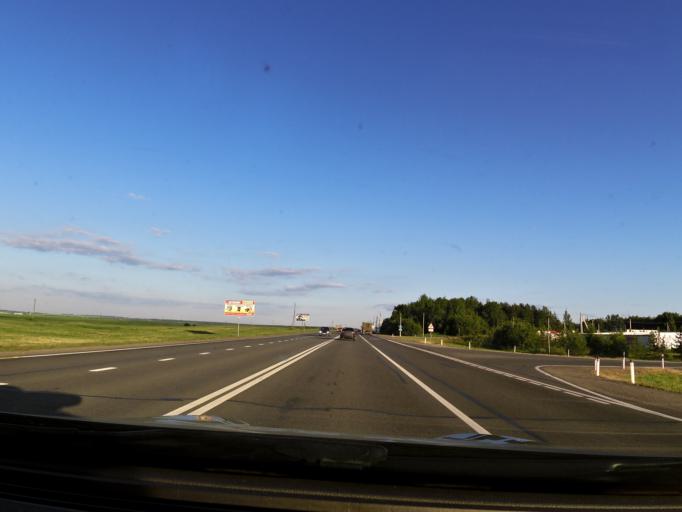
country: RU
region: Vologda
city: Vologda
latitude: 59.1572
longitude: 39.9301
